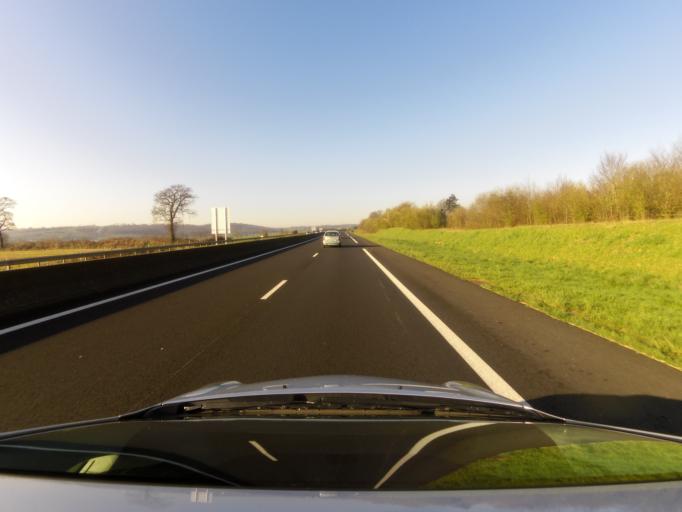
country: FR
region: Lower Normandy
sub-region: Departement du Calvados
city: Villers-Bocage
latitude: 49.0580
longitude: -0.6977
